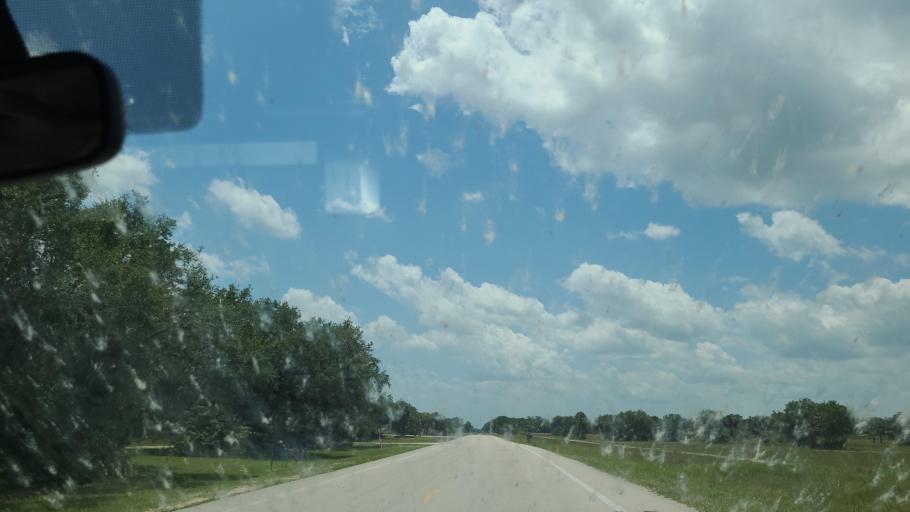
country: US
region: Florida
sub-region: Glades County
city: Buckhead Ridge
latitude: 27.1007
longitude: -81.0699
